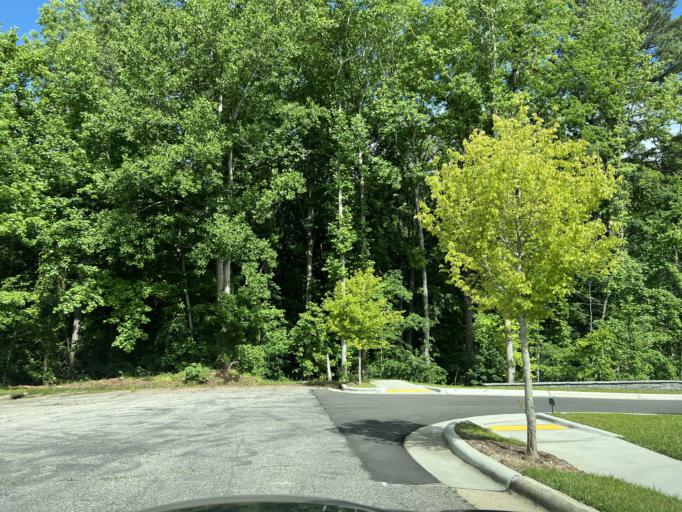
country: US
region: North Carolina
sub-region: Wake County
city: Wake Forest
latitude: 35.8934
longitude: -78.5676
